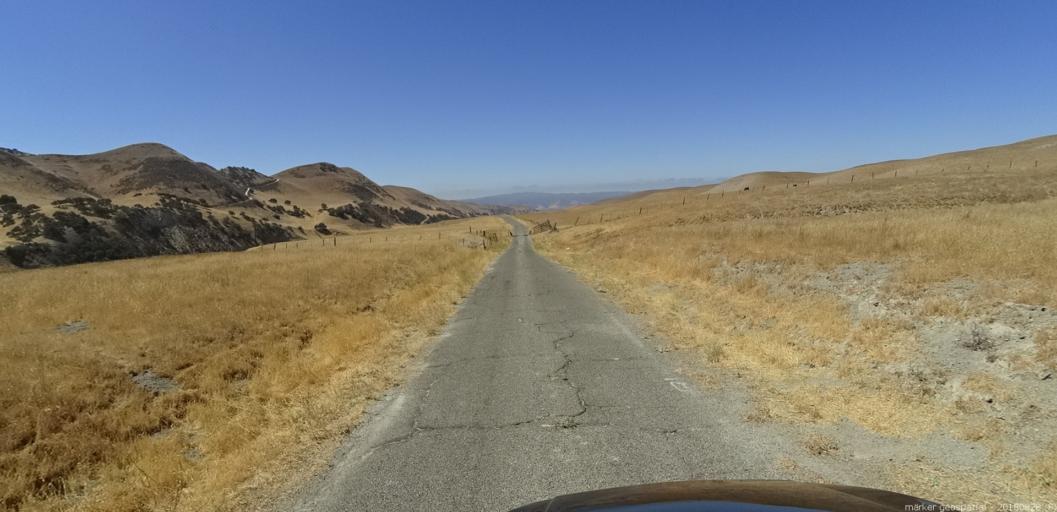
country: US
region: California
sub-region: San Luis Obispo County
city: San Miguel
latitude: 36.0570
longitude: -120.8095
